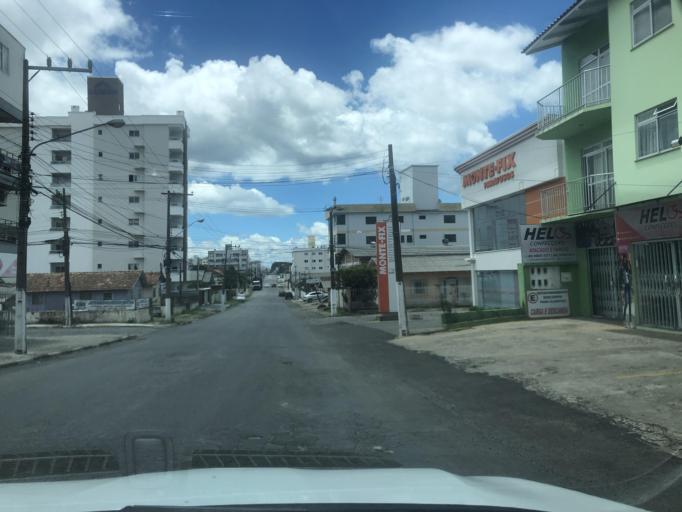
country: BR
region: Santa Catarina
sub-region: Lages
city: Lages
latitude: -27.8077
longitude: -50.3019
